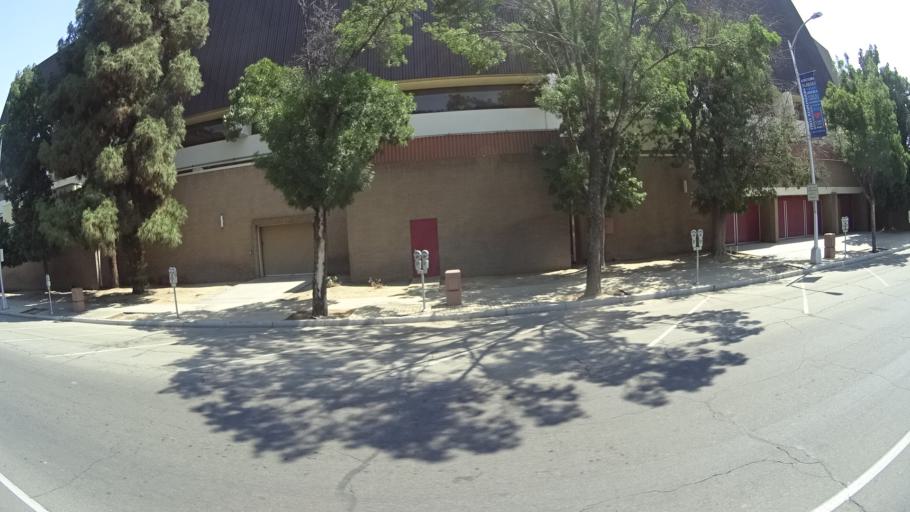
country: US
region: California
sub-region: Fresno County
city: Fresno
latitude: 36.7326
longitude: -119.7833
